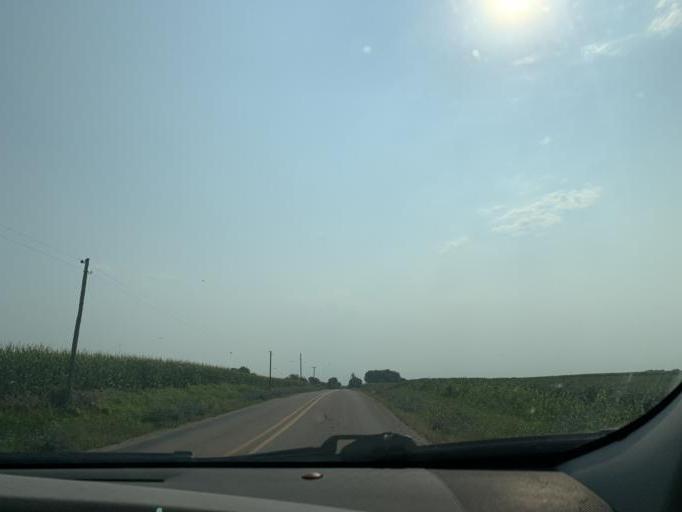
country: US
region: Illinois
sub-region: Carroll County
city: Milledgeville
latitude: 41.8479
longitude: -89.8167
